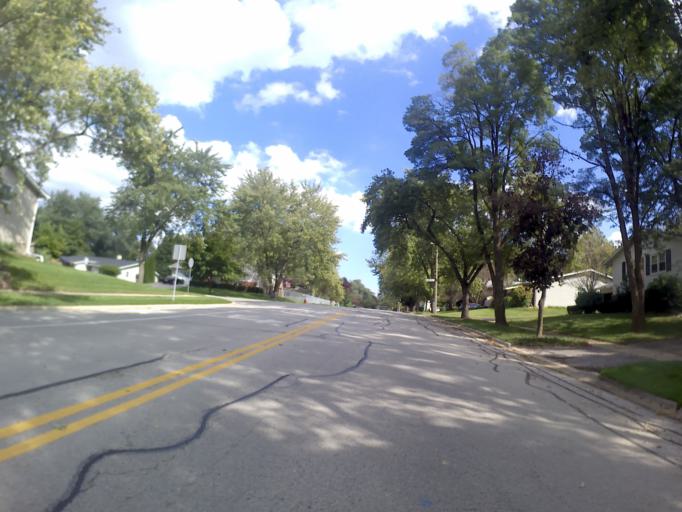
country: US
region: Illinois
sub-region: DuPage County
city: Woodridge
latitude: 41.7687
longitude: -88.0677
